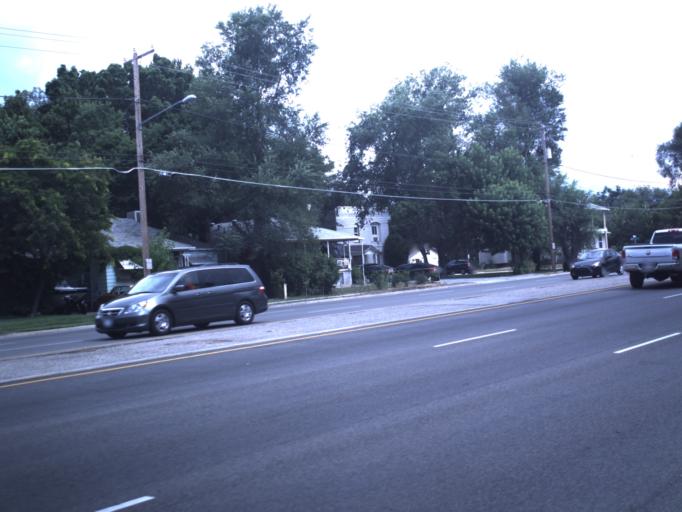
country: US
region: Utah
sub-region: Salt Lake County
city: South Salt Lake
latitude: 40.7098
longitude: -111.8715
